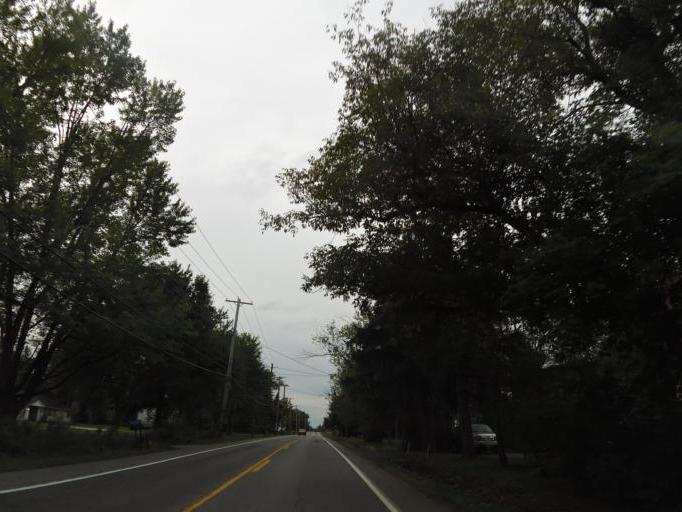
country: US
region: New York
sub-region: Erie County
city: Elma Center
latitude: 42.8131
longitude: -78.6367
